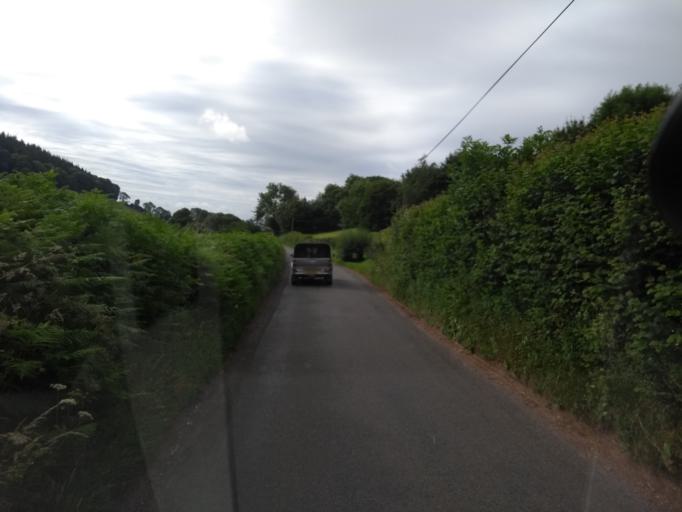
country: GB
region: England
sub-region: Somerset
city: Wiveliscombe
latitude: 51.0963
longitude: -3.3037
